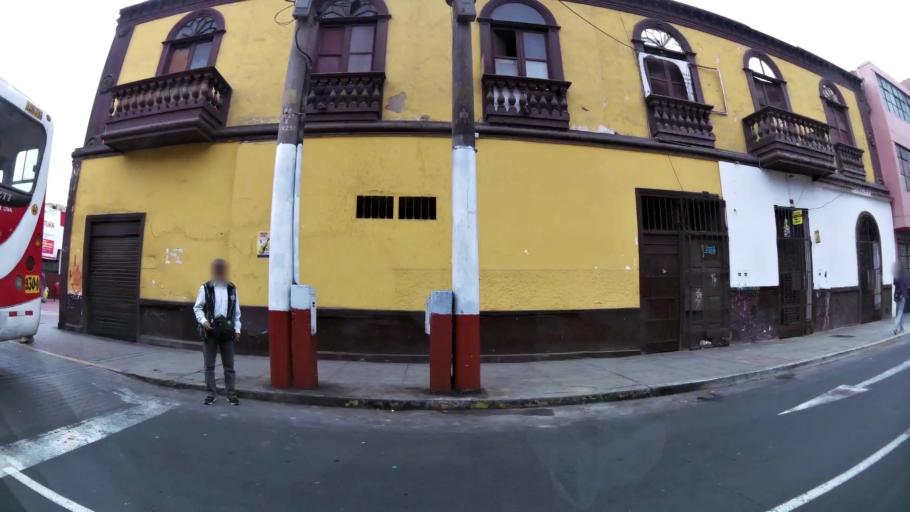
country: PE
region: Callao
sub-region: Callao
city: Callao
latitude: -12.0625
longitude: -77.1455
